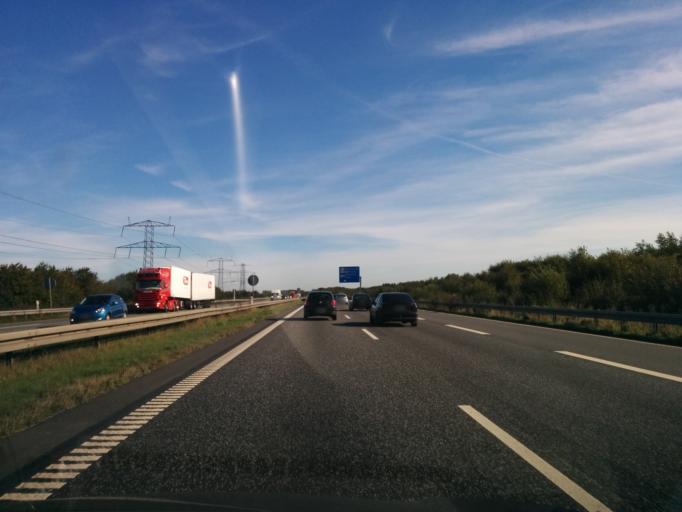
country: DK
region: South Denmark
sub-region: Kolding Kommune
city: Kolding
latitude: 55.5310
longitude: 9.4833
